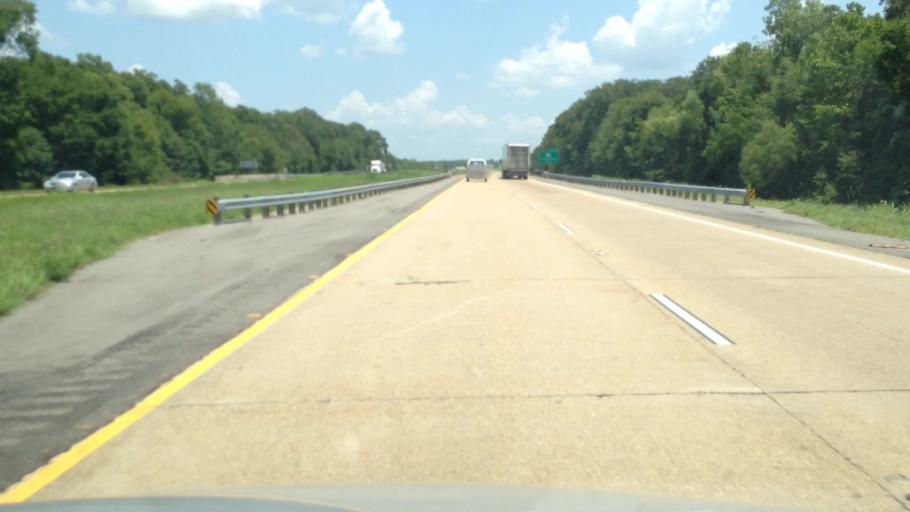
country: US
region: Louisiana
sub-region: Rapides Parish
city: Lecompte
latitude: 30.9939
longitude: -92.3240
